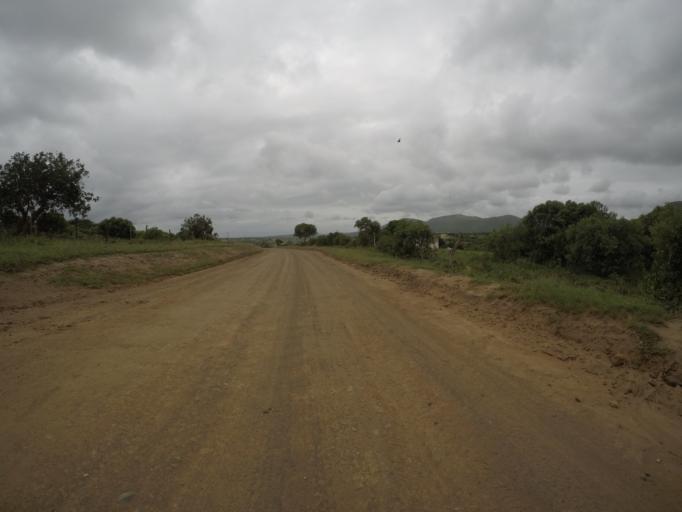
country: ZA
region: KwaZulu-Natal
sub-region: uThungulu District Municipality
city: Empangeni
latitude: -28.5956
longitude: 31.8394
